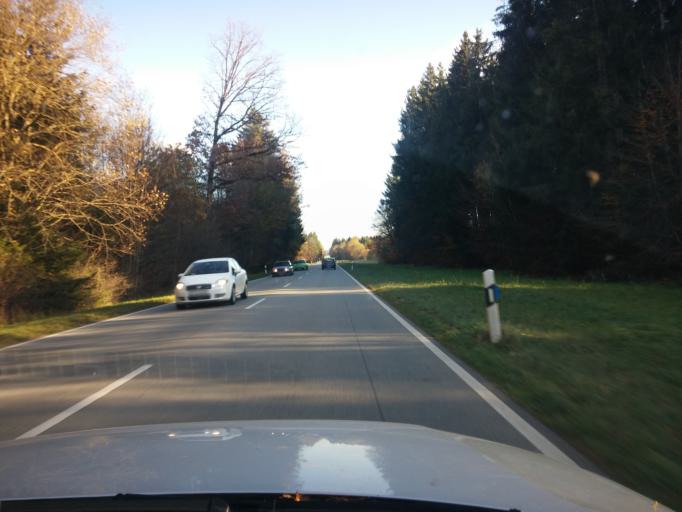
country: DE
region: Bavaria
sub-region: Upper Bavaria
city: Aying
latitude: 47.9856
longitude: 11.7430
